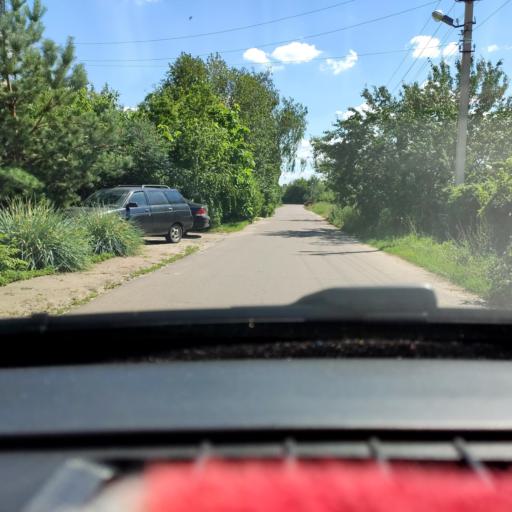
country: RU
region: Voronezj
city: Maslovka
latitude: 51.5487
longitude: 39.2479
